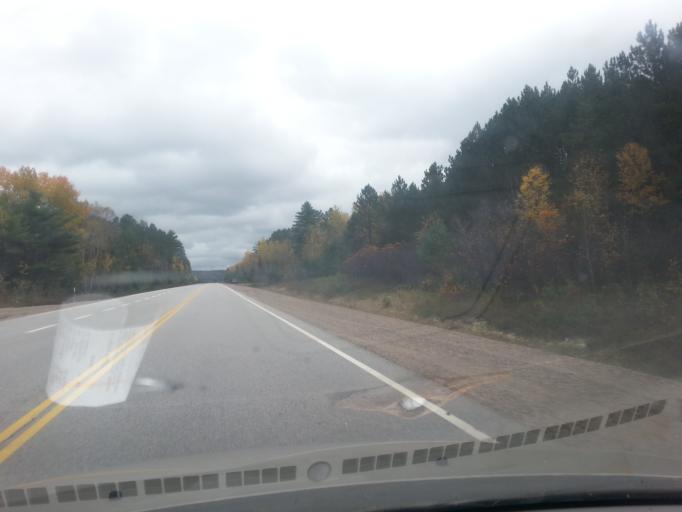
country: CA
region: Ontario
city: Mattawa
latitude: 46.2825
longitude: -78.4119
